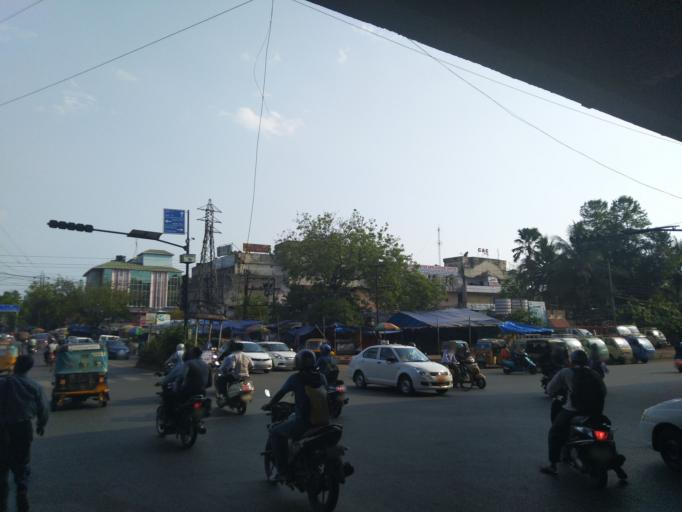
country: IN
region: Odisha
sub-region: Khordha
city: Bhubaneshwar
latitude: 20.2850
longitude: 85.8079
